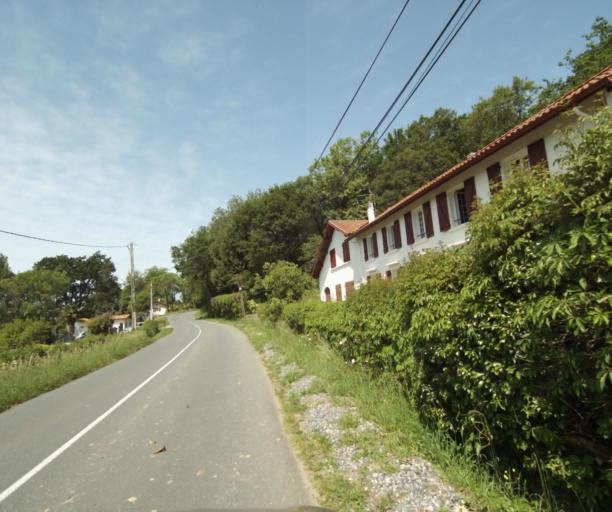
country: FR
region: Aquitaine
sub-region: Departement des Pyrenees-Atlantiques
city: Mouguerre
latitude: 43.4547
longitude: -1.4269
